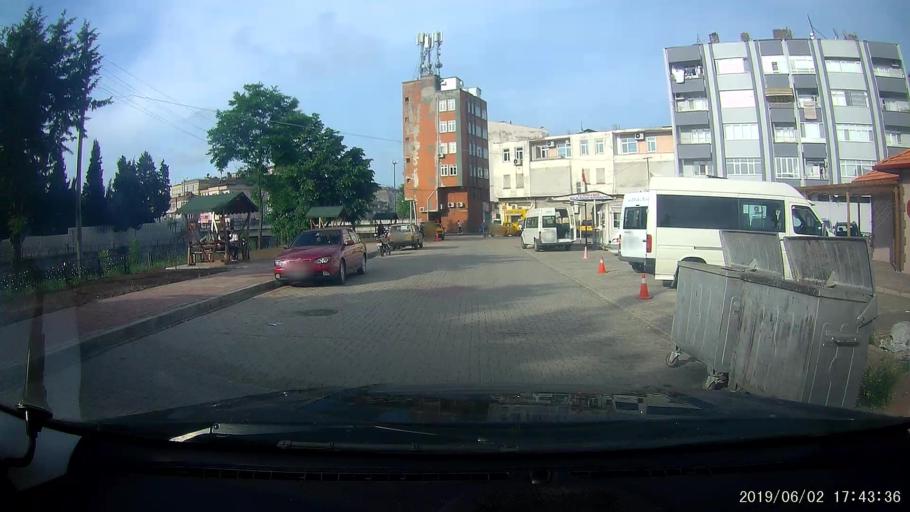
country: TR
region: Samsun
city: Terme
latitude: 41.2074
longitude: 36.9716
